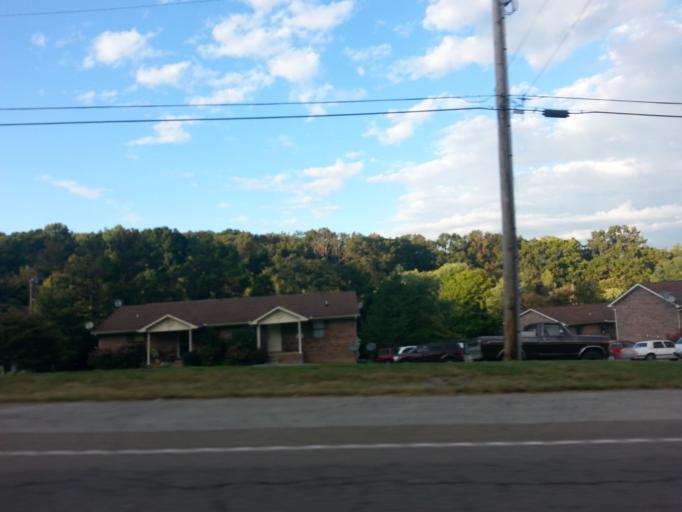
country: US
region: Tennessee
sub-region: Jefferson County
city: Jefferson City
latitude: 36.1259
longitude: -83.5172
